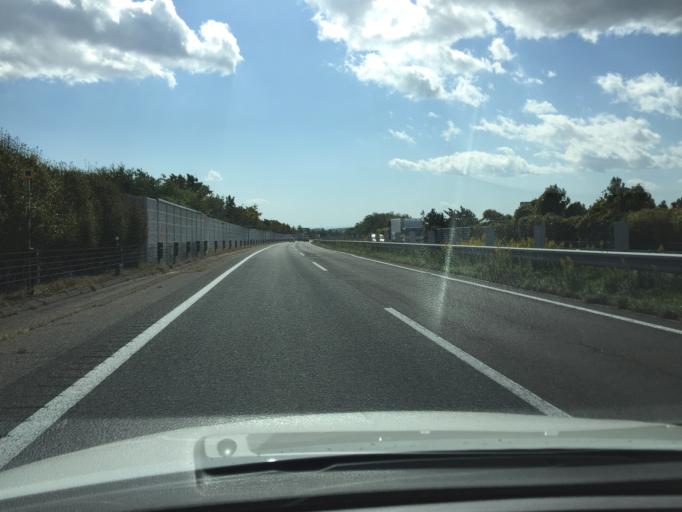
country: JP
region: Fukushima
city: Koriyama
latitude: 37.3841
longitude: 140.3128
